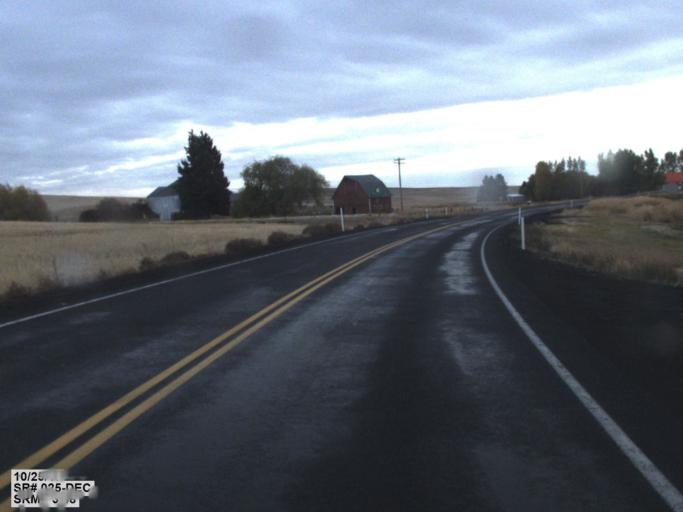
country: US
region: Washington
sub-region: Lincoln County
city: Davenport
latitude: 47.7050
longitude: -118.1422
